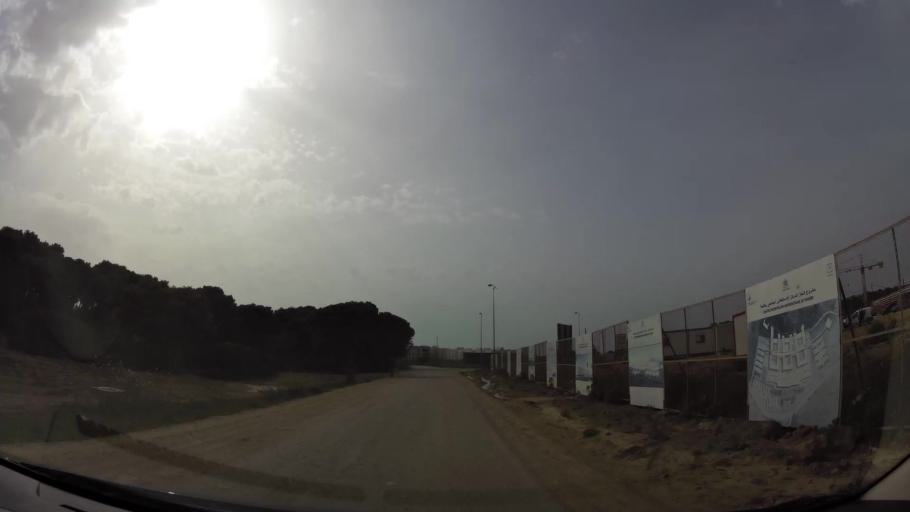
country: MA
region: Tanger-Tetouan
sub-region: Tanger-Assilah
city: Boukhalef
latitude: 35.6823
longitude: -5.9263
